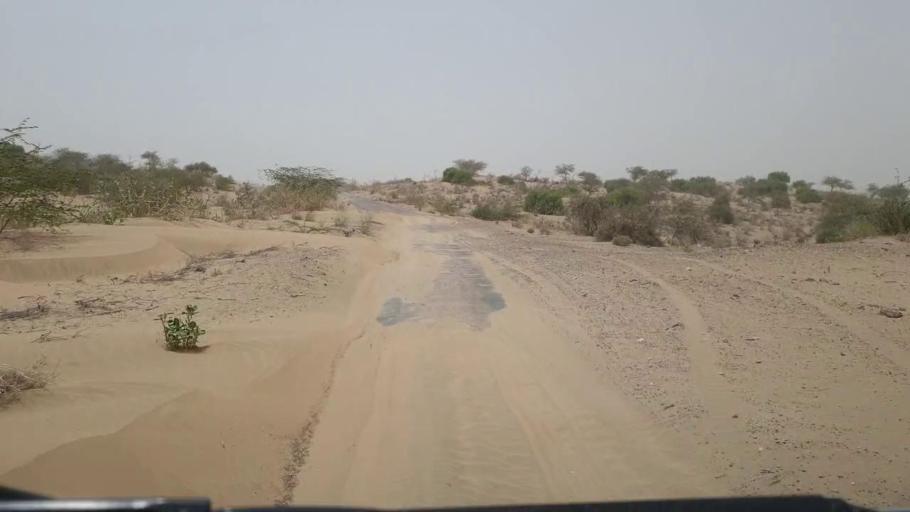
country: PK
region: Sindh
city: Naukot
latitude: 24.7781
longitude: 69.5365
